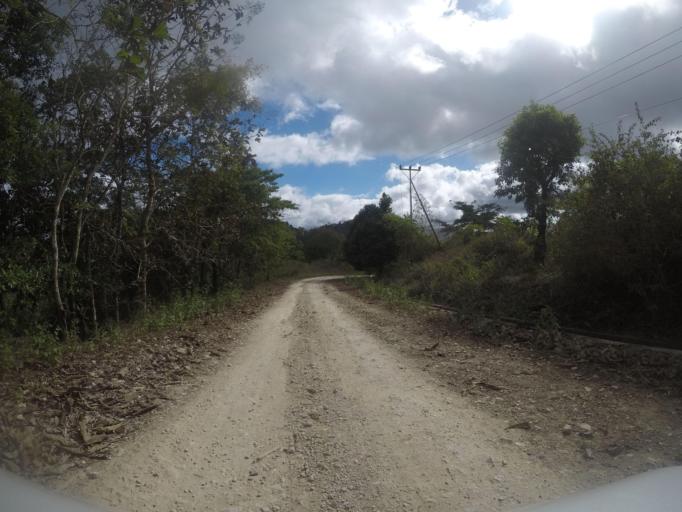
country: TL
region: Lautem
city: Lospalos
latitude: -8.5451
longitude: 126.9047
